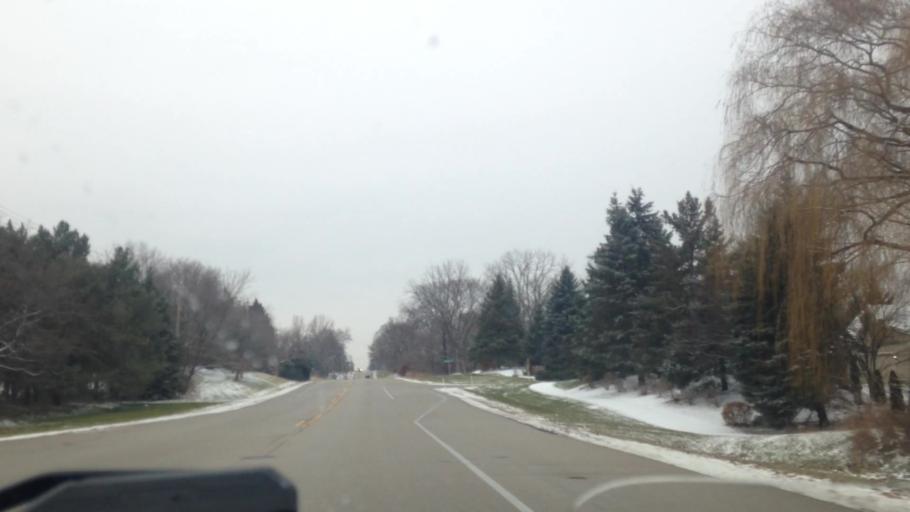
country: US
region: Wisconsin
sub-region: Waukesha County
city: Brookfield
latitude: 43.0941
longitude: -88.1059
